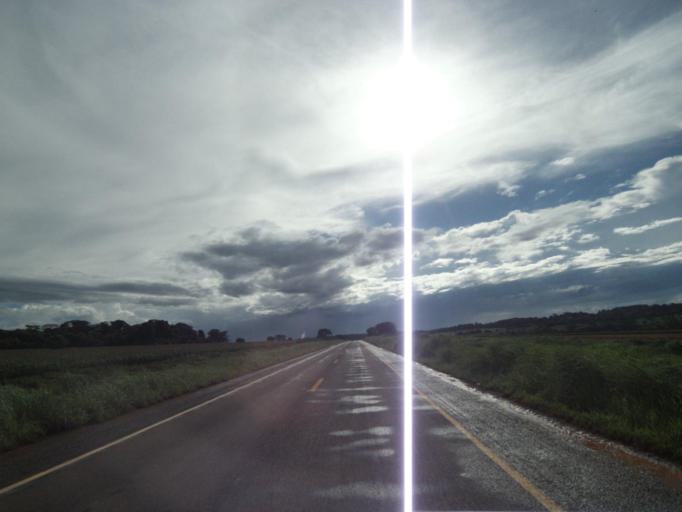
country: BR
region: Goias
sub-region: Jaragua
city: Jaragua
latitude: -15.9042
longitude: -49.5454
